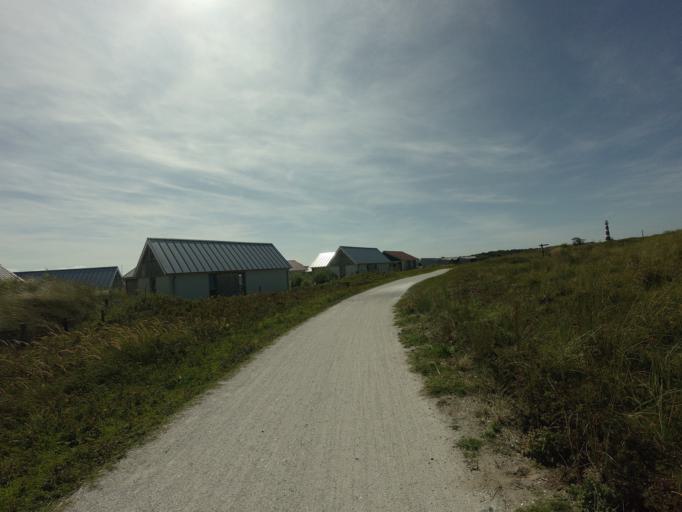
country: NL
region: Friesland
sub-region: Gemeente Ameland
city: Hollum
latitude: 53.4519
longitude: 5.6356
